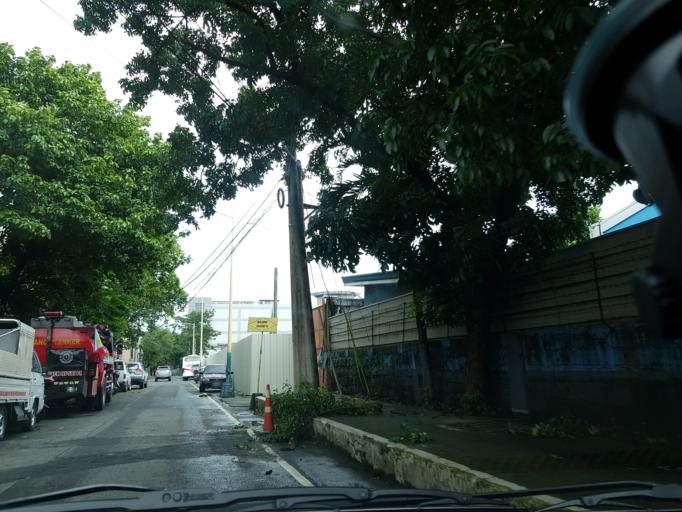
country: PH
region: Metro Manila
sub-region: Pasig
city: Pasig City
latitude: 14.5678
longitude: 121.0695
